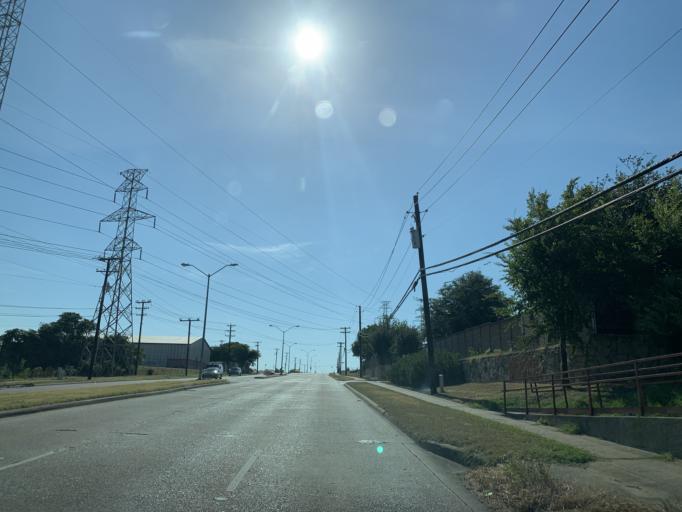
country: US
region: Texas
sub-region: Dallas County
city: Cockrell Hill
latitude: 32.7059
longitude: -96.8939
